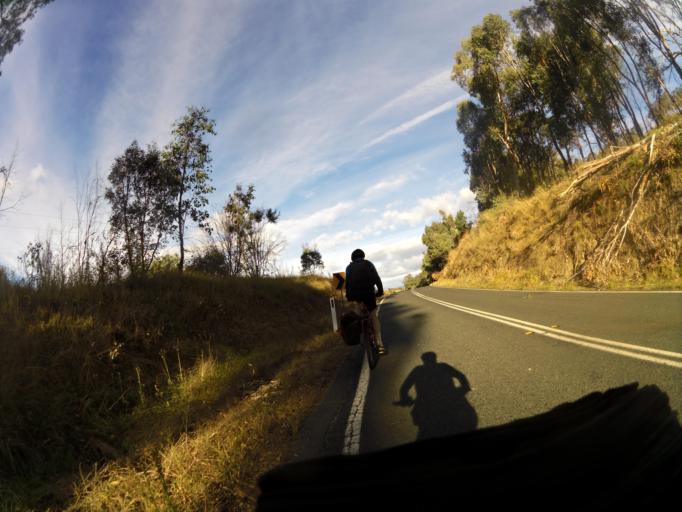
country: AU
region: New South Wales
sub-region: Greater Hume Shire
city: Holbrook
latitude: -36.0018
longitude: 147.8746
